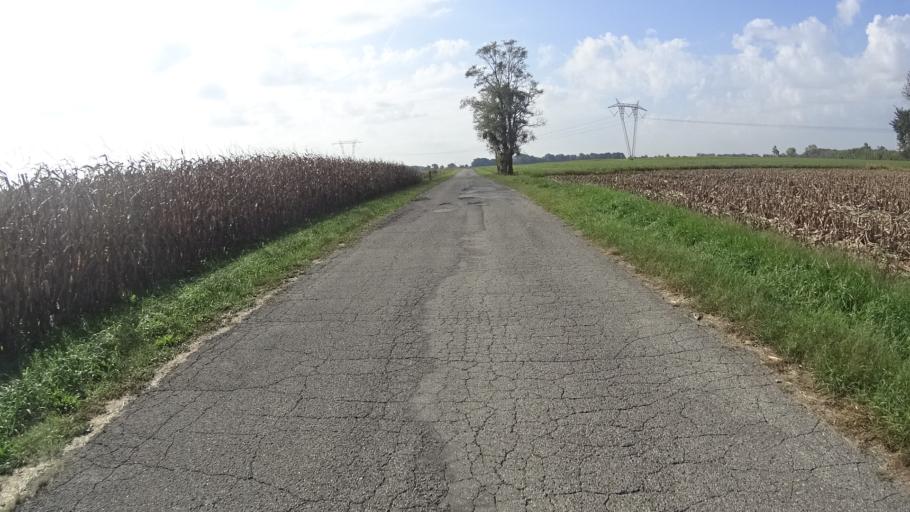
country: US
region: Indiana
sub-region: Madison County
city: Ingalls
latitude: 40.0086
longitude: -85.8243
